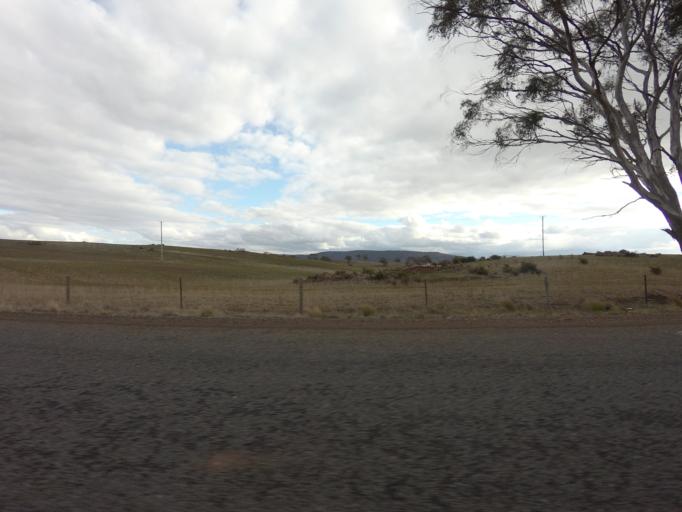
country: AU
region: Tasmania
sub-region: Northern Midlands
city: Evandale
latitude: -41.9071
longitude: 147.4574
